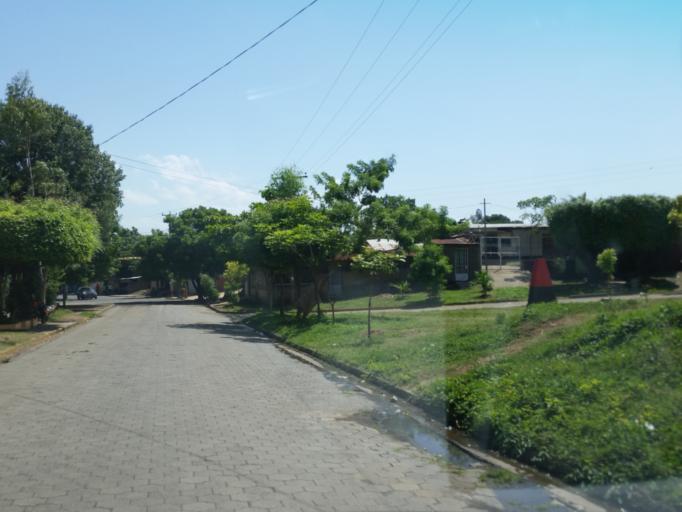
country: NI
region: Managua
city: Managua
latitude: 12.1040
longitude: -86.2239
